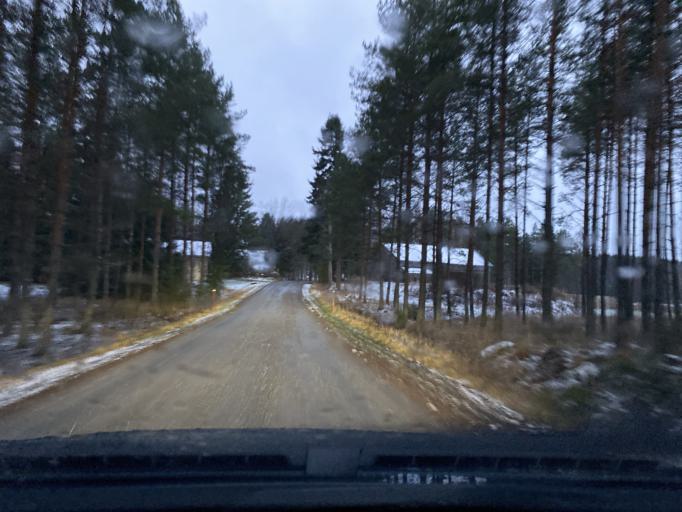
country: FI
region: Pirkanmaa
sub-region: Lounais-Pirkanmaa
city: Punkalaidun
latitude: 61.1634
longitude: 22.9638
